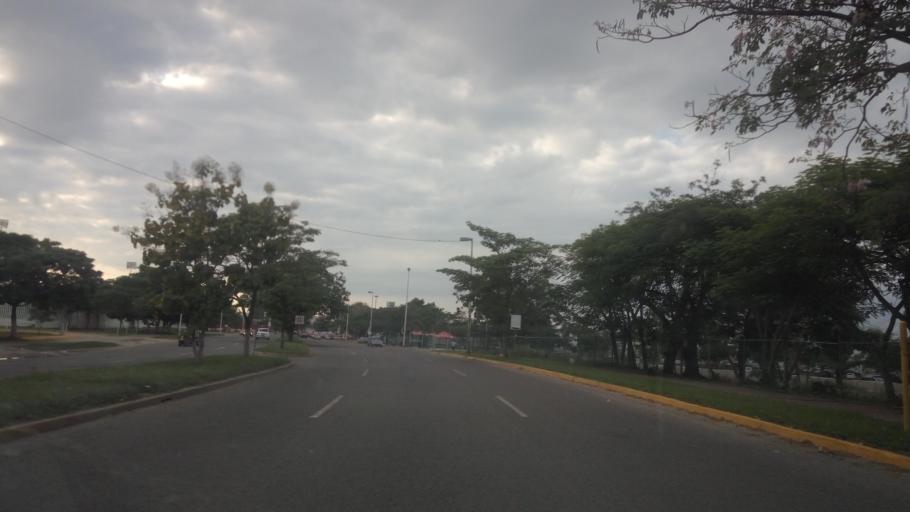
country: MX
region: Tabasco
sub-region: Nacajuca
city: Bosque de Saloya
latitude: 18.0051
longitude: -92.9611
